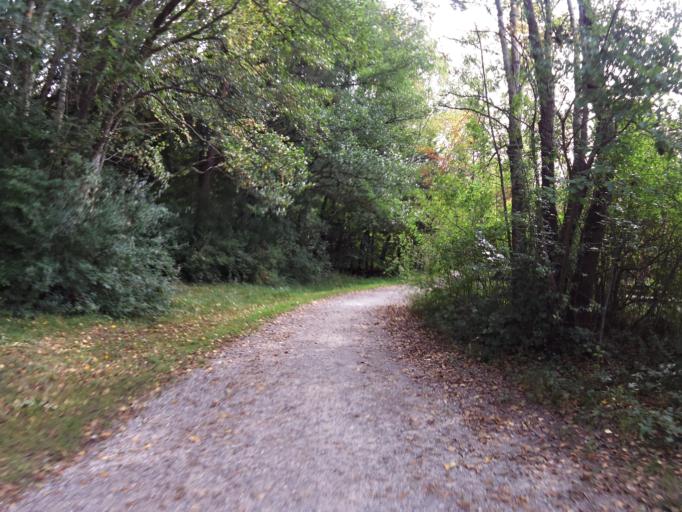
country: DE
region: Bavaria
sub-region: Upper Bavaria
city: Seeshaupt
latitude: 47.8423
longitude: 11.3381
